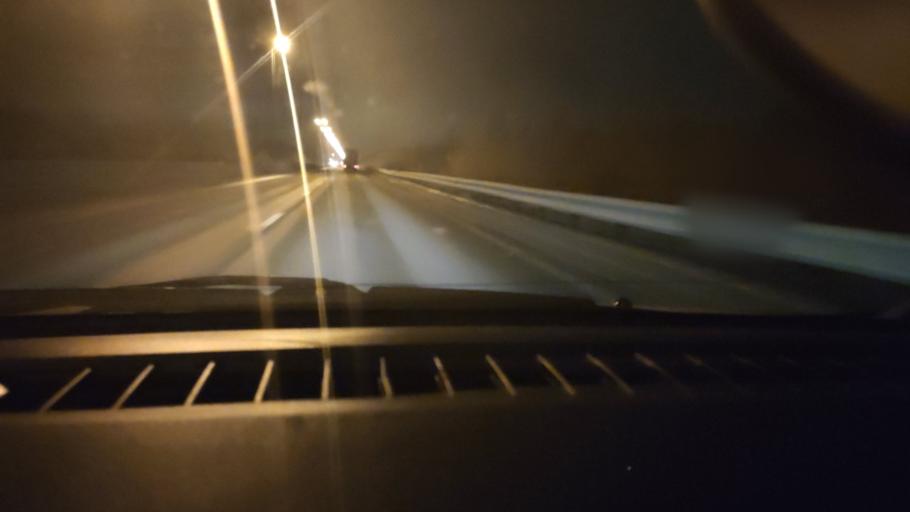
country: RU
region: Perm
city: Kondratovo
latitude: 57.9906
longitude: 56.0646
